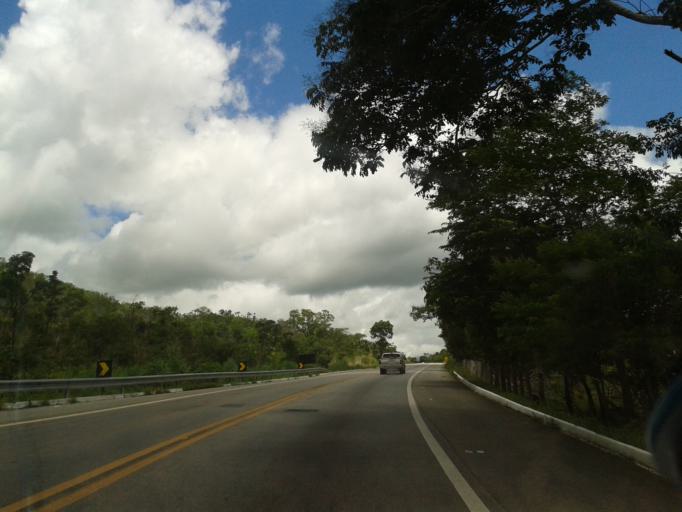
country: BR
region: Goias
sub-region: Goias
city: Goias
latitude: -15.8796
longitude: -50.1017
